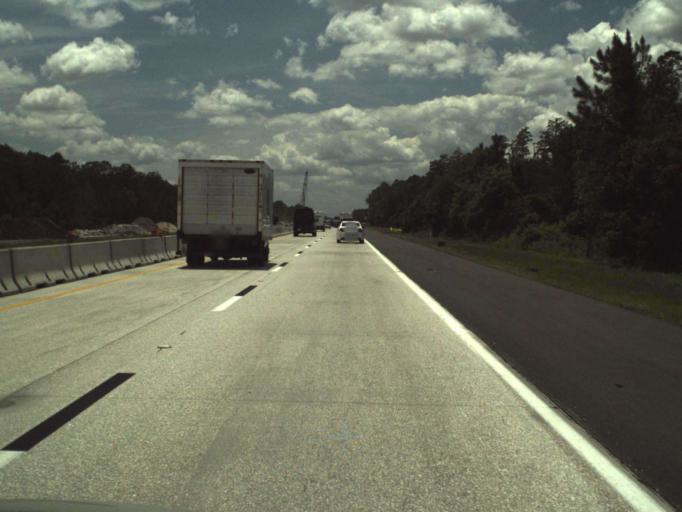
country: US
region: Florida
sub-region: Volusia County
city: Samsula-Spruce Creek
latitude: 29.0834
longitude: -81.1697
